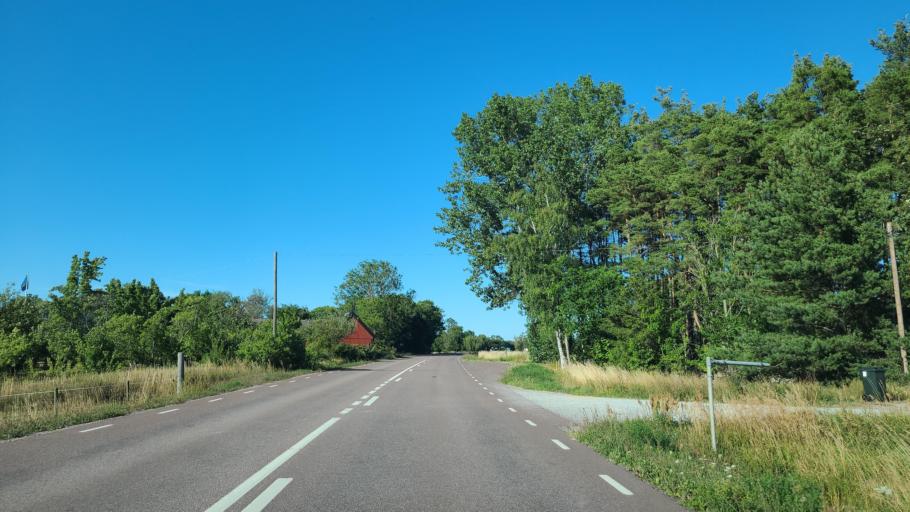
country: SE
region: Kalmar
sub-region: Borgholms Kommun
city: Borgholm
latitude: 57.1900
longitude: 17.0316
